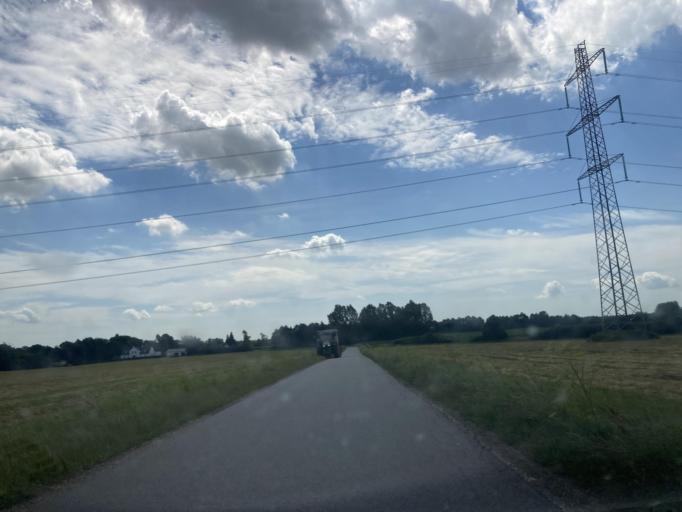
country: DK
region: Zealand
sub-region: Koge Kommune
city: Borup
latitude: 55.4534
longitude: 11.9489
